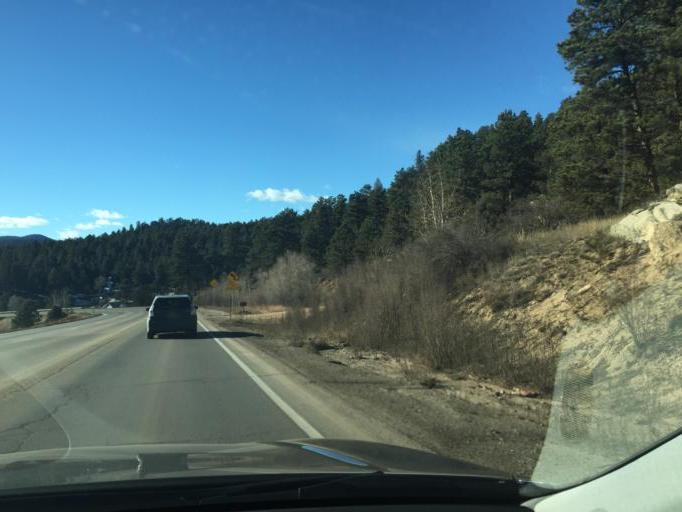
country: US
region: Colorado
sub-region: Jefferson County
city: Evergreen
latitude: 39.4884
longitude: -105.3574
